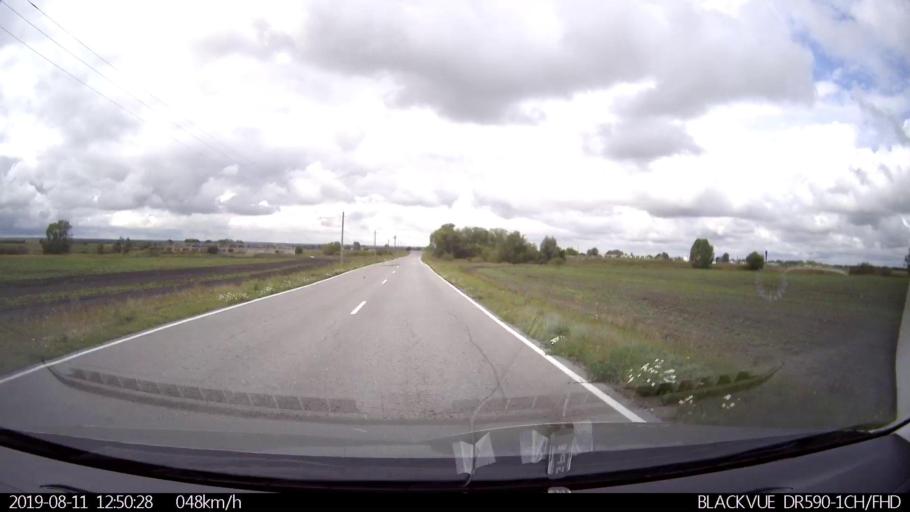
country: RU
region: Ulyanovsk
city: Ignatovka
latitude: 53.8751
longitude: 47.6731
